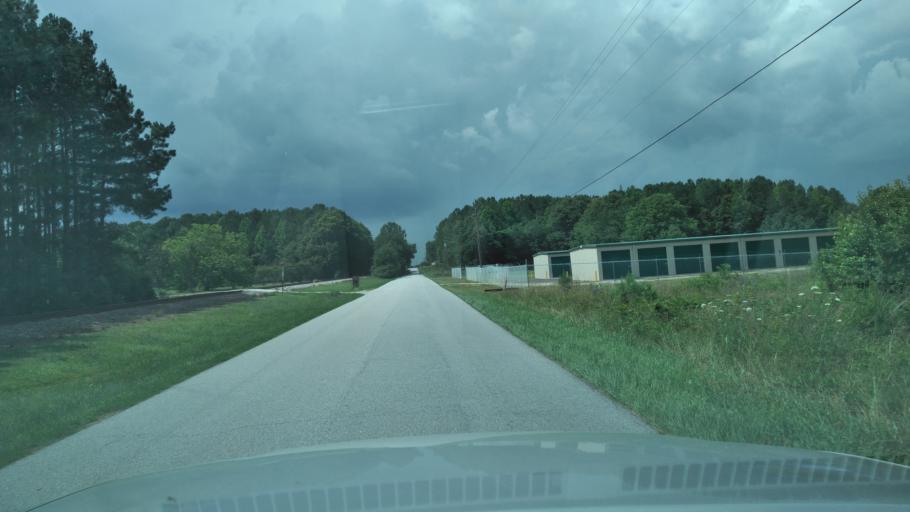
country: US
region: South Carolina
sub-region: Laurens County
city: Laurens
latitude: 34.5631
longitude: -82.0846
